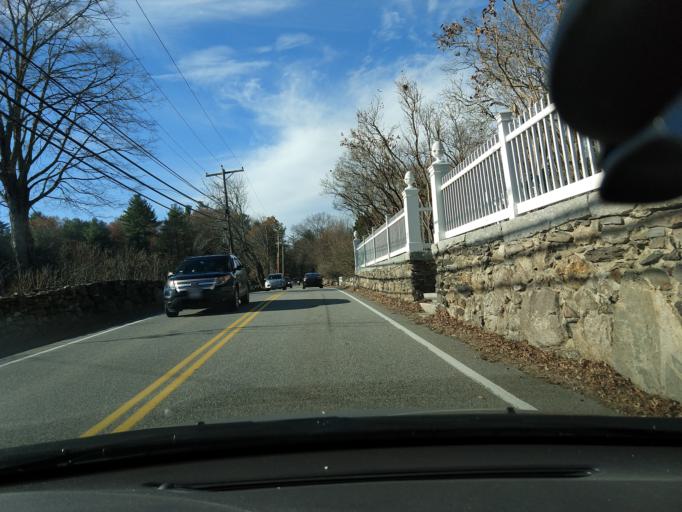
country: US
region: Massachusetts
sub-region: Middlesex County
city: Dunstable
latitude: 42.6818
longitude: -71.4599
